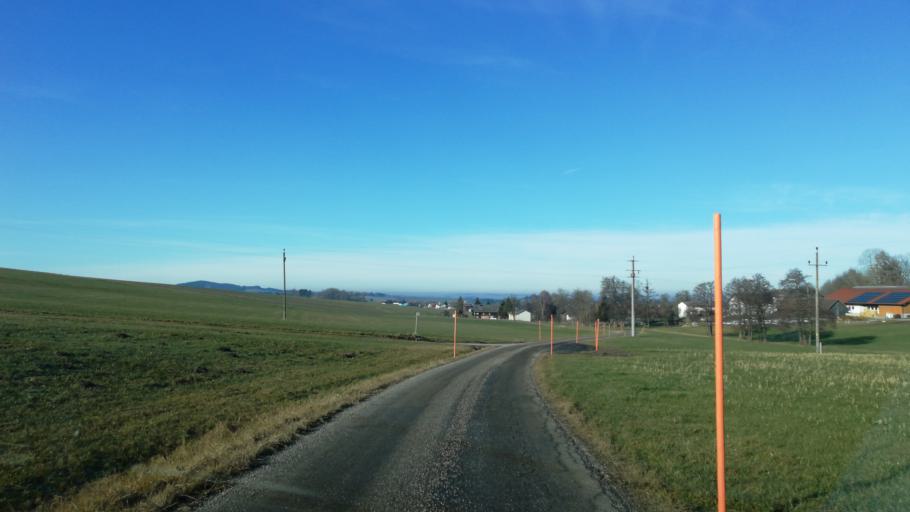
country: AT
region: Upper Austria
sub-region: Politischer Bezirk Vocklabruck
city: Zell am Pettenfirst
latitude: 48.1460
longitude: 13.5906
